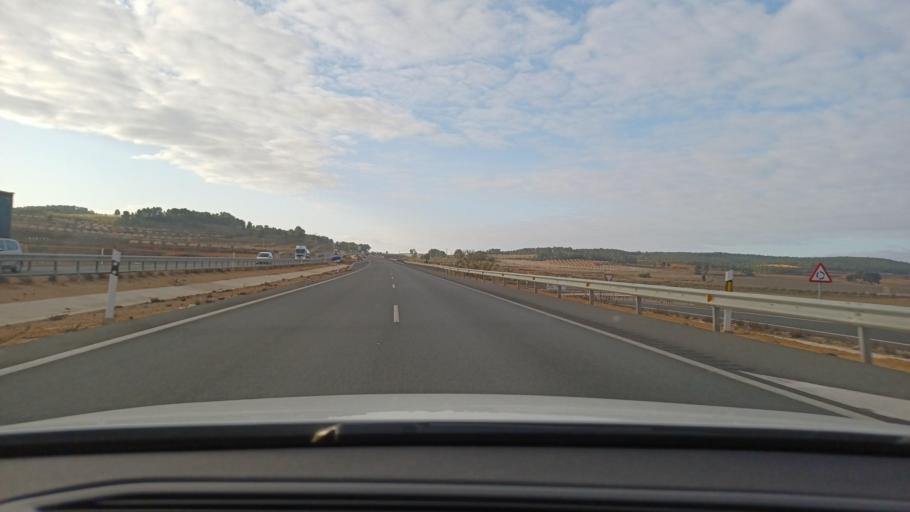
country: ES
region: Valencia
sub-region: Provincia de Valencia
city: La Font de la Figuera
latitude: 38.7856
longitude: -0.8927
